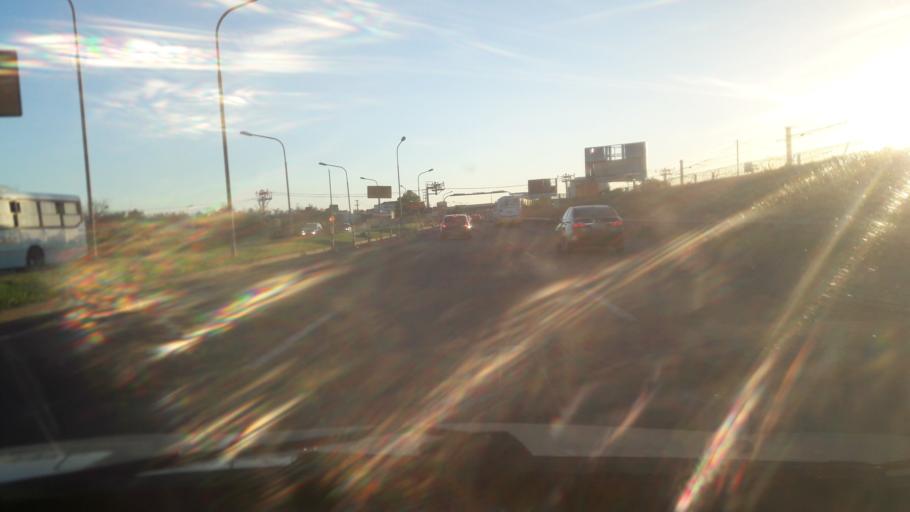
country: BR
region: Rio Grande do Sul
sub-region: Porto Alegre
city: Porto Alegre
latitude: -29.9934
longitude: -51.1870
